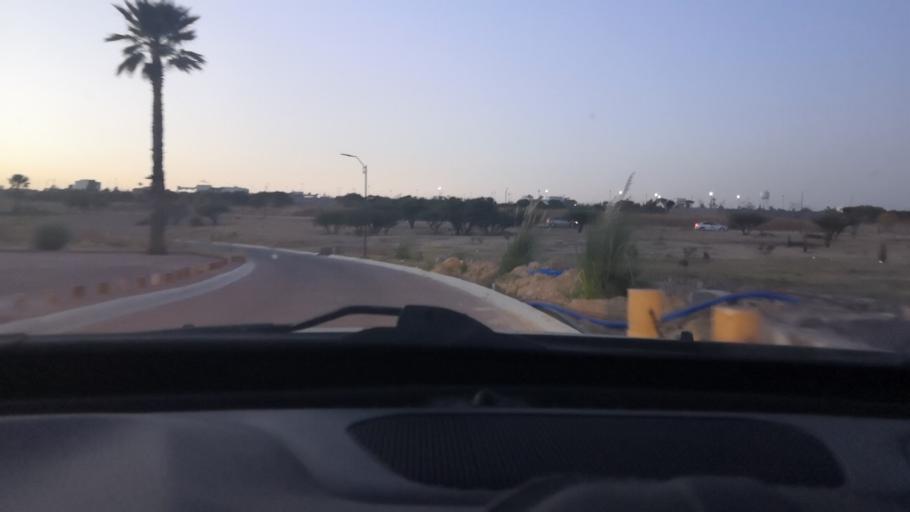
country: MX
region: Guanajuato
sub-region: Leon
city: Fraccionamiento Paseo de las Torres
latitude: 21.2290
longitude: -101.8057
